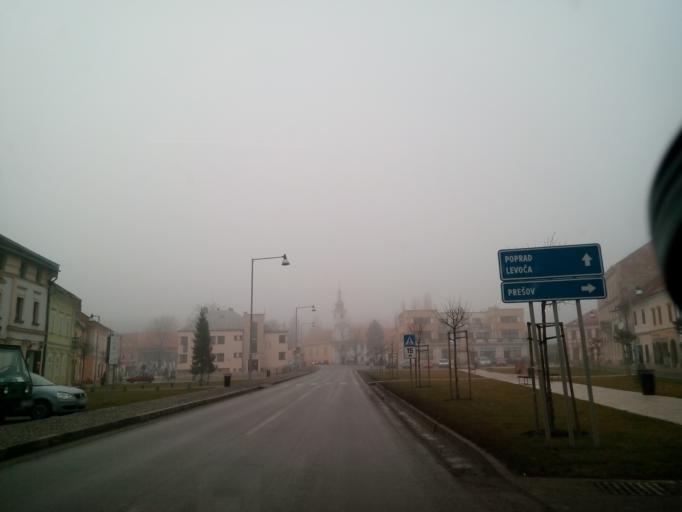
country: SK
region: Presovsky
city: Spisske Podhradie
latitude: 48.9998
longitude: 20.7534
